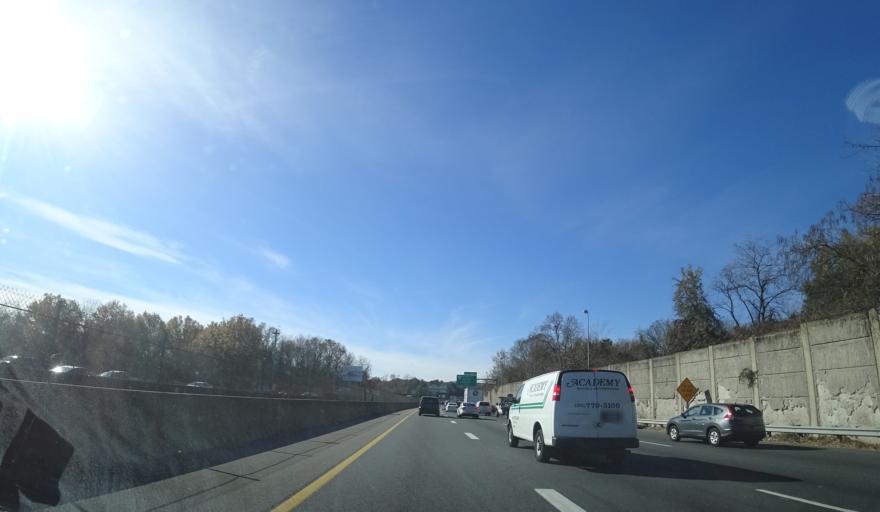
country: US
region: Virginia
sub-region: Fairfax County
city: Merrifield
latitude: 38.8812
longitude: -77.2353
